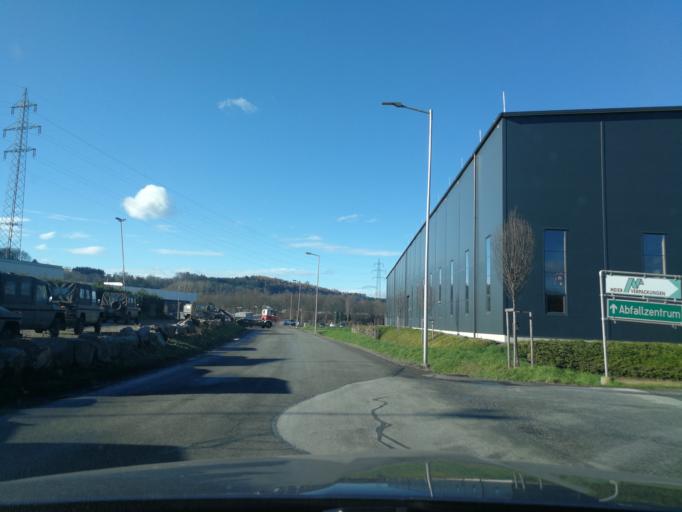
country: AT
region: Styria
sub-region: Politischer Bezirk Weiz
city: Gleisdorf
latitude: 47.1173
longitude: 15.6974
